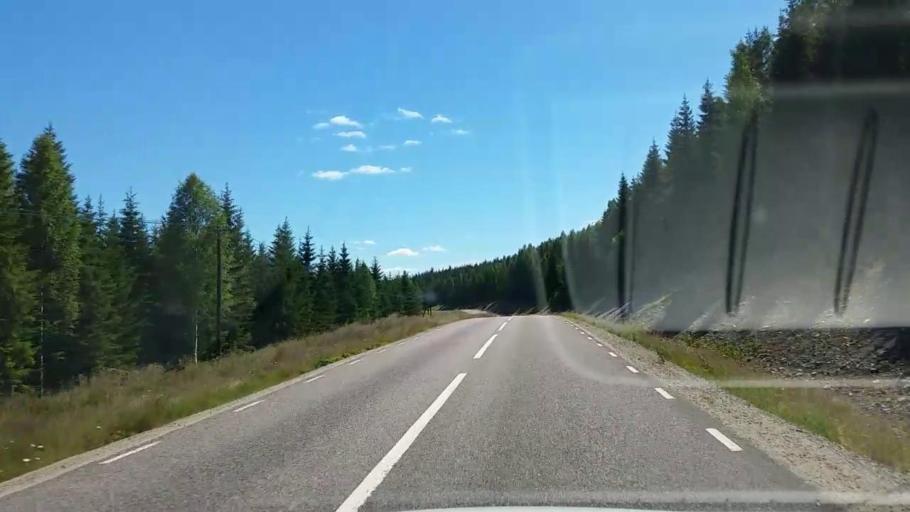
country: SE
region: Gaevleborg
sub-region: Ovanakers Kommun
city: Edsbyn
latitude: 61.5788
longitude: 15.6608
